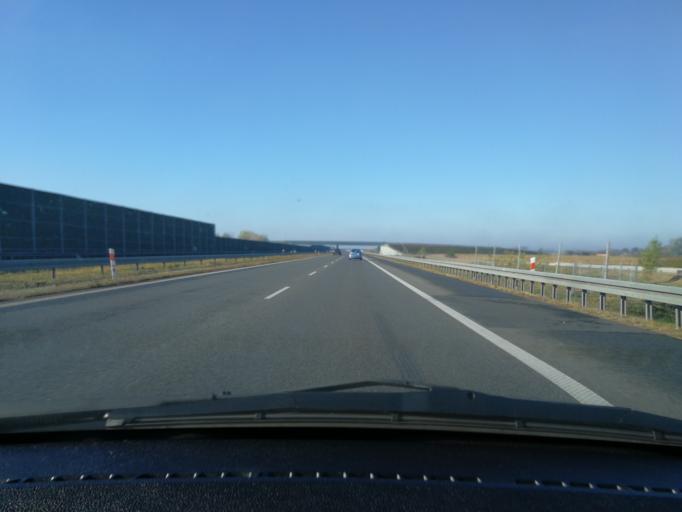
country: PL
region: Masovian Voivodeship
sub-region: Powiat warszawski zachodni
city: Bieniewice
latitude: 52.1382
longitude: 20.5764
